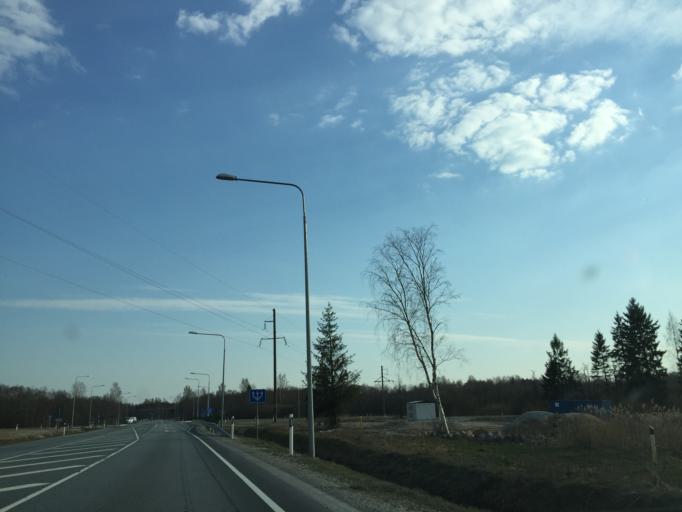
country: EE
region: Jogevamaa
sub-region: Mustvee linn
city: Mustvee
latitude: 58.8492
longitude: 26.9136
